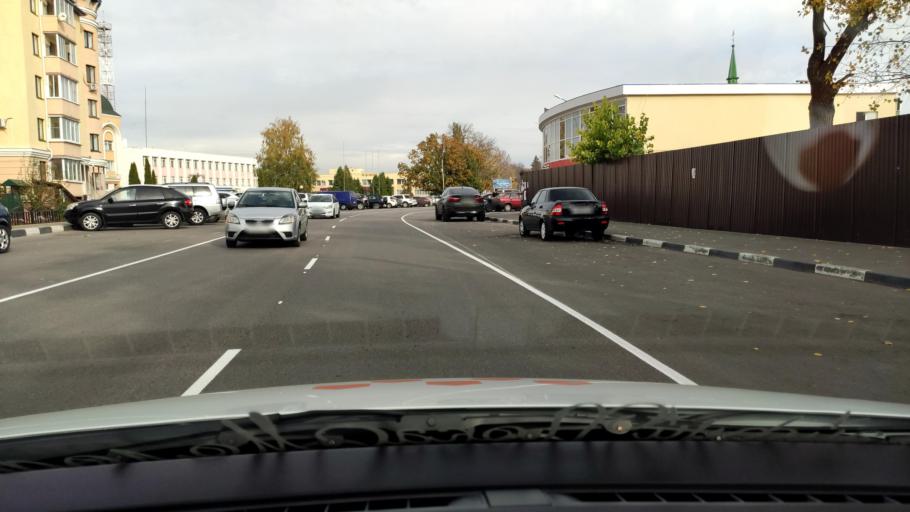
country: RU
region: Voronezj
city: Ramon'
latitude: 51.9112
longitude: 39.3384
